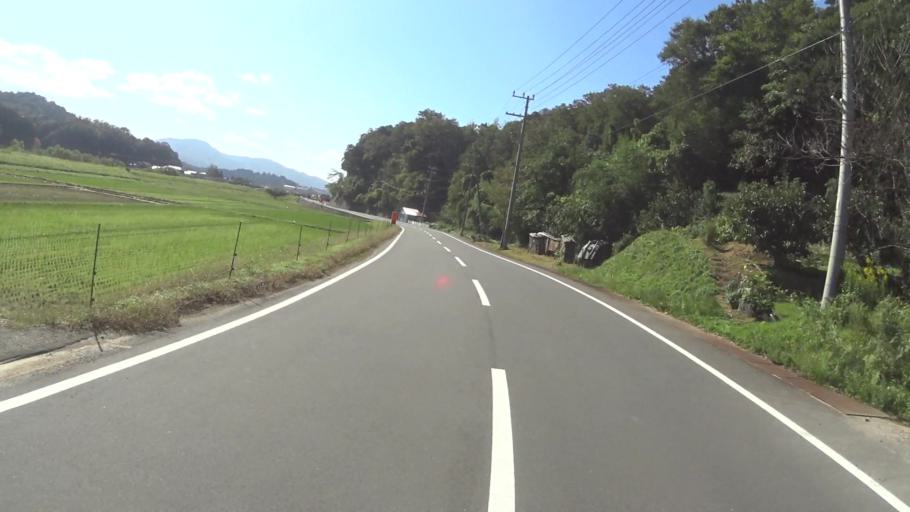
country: JP
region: Kyoto
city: Miyazu
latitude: 35.6921
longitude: 135.0970
